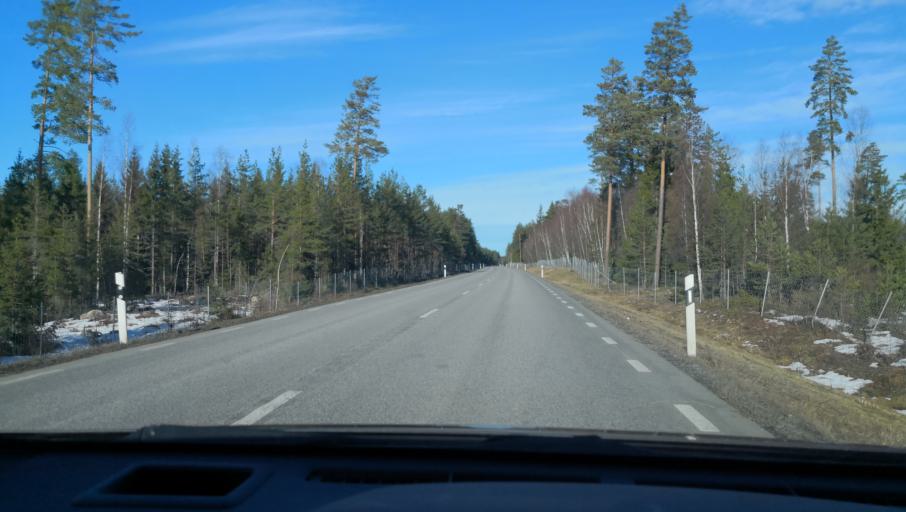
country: SE
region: Uppsala
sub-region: Uppsala Kommun
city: Vattholma
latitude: 60.0432
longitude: 17.7512
